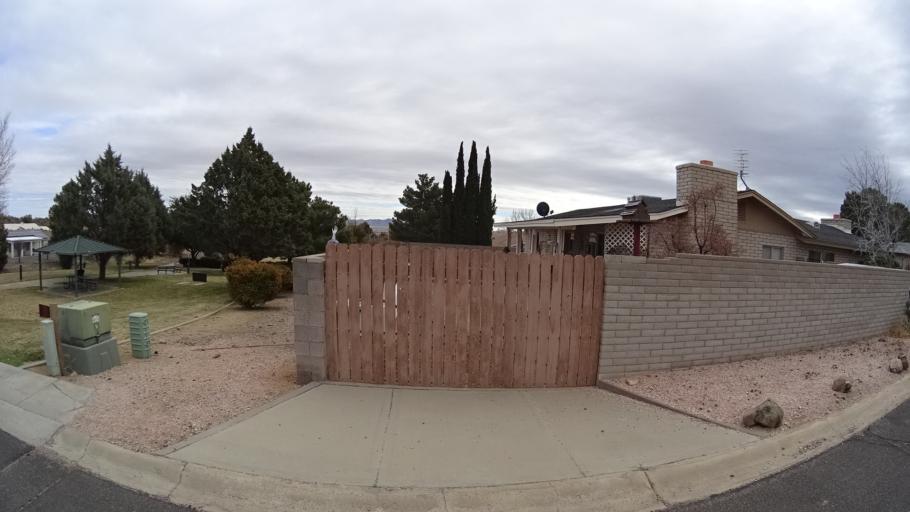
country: US
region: Arizona
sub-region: Mohave County
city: New Kingman-Butler
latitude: 35.2385
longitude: -114.0491
